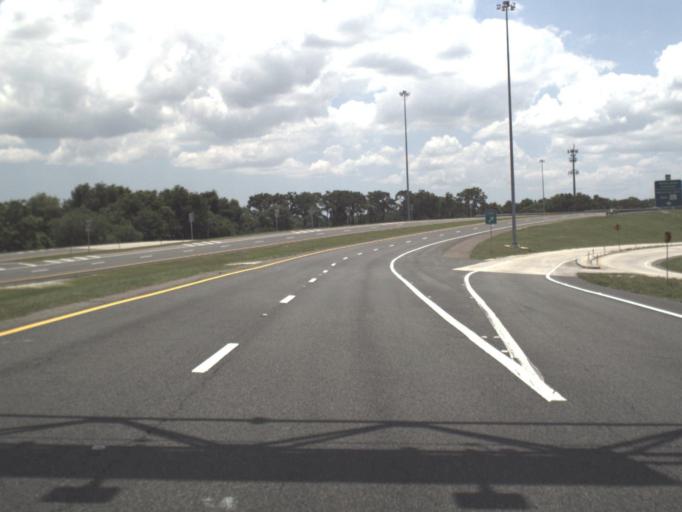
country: US
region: Florida
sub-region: Duval County
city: Jacksonville
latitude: 30.3556
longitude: -81.5535
